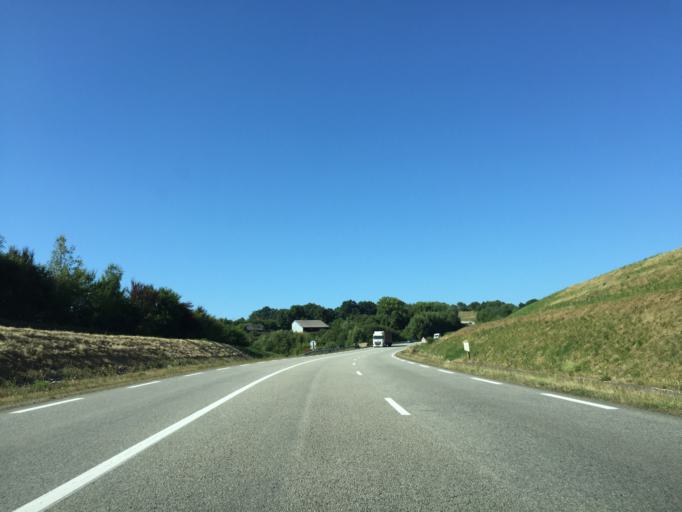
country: FR
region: Lower Normandy
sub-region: Departement du Calvados
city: Lisieux
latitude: 49.1822
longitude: 0.2271
